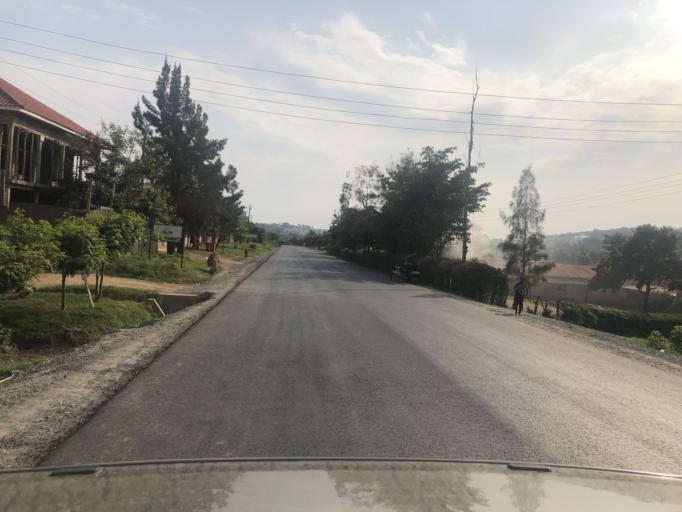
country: UG
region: Western Region
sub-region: Rubirizi District
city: Rubirizi
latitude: -0.2411
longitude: 30.0933
